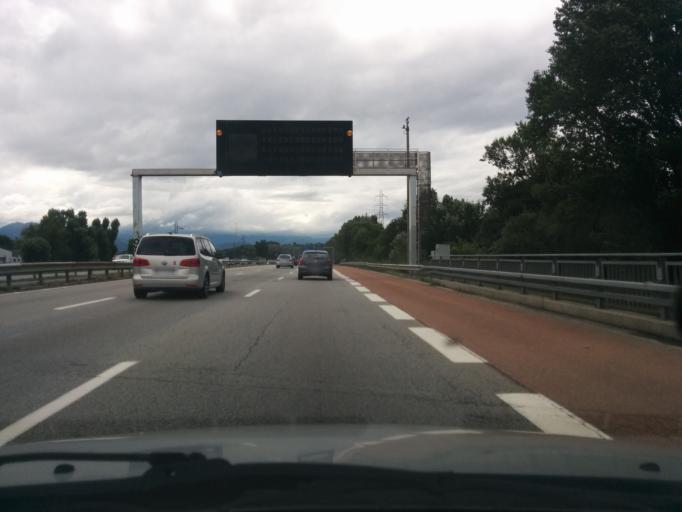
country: FR
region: Rhone-Alpes
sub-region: Departement de l'Isere
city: Saint-Egreve
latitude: 45.2246
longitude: 5.6697
